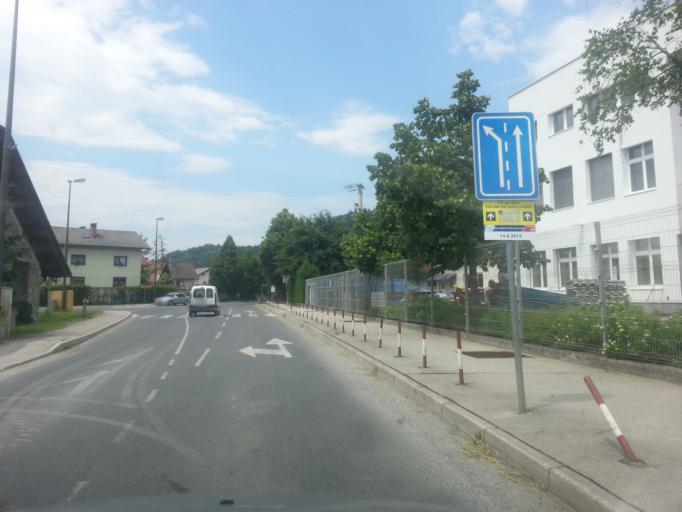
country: SI
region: Horjul
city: Horjul
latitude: 46.0222
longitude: 14.3008
